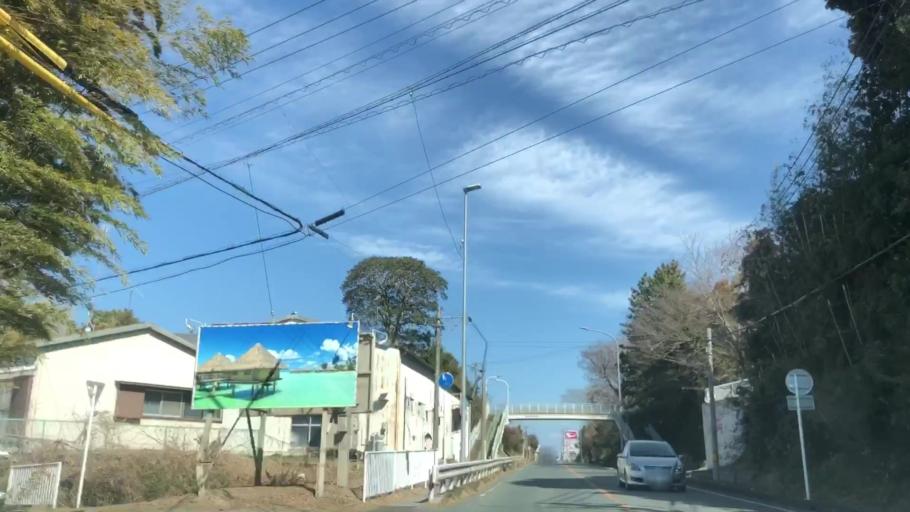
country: JP
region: Aichi
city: Toyohashi
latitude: 34.7218
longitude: 137.3730
